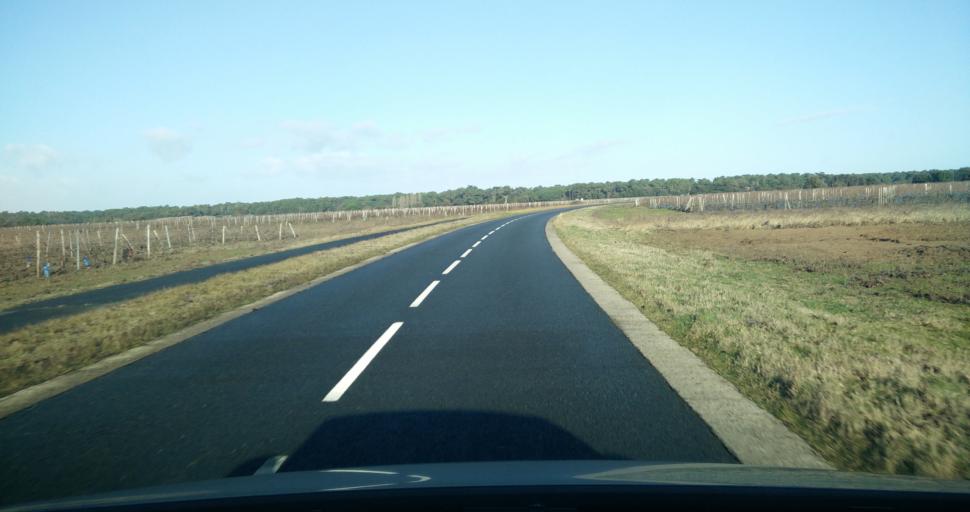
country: FR
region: Poitou-Charentes
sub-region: Departement de la Charente-Maritime
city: Sainte-Marie-de-Re
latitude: 46.1620
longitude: -1.3211
